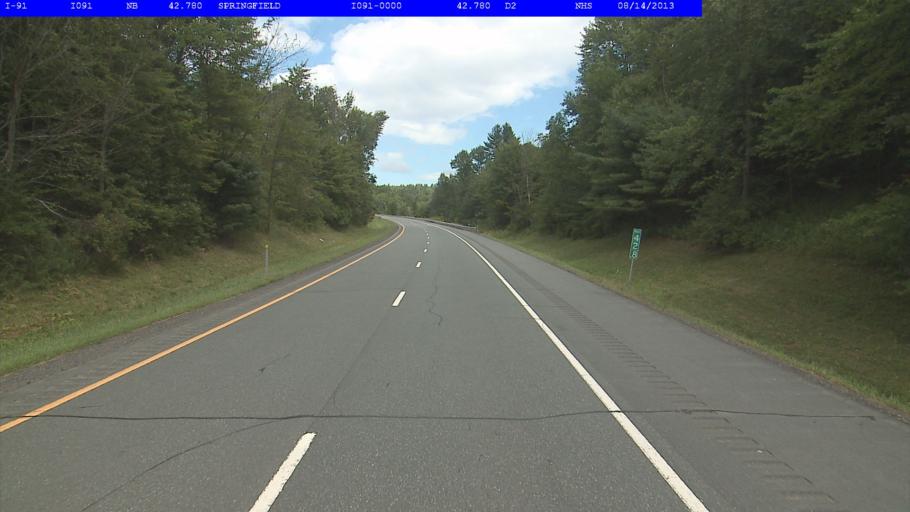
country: US
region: New Hampshire
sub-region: Sullivan County
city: Charlestown
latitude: 43.2813
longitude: -72.4297
